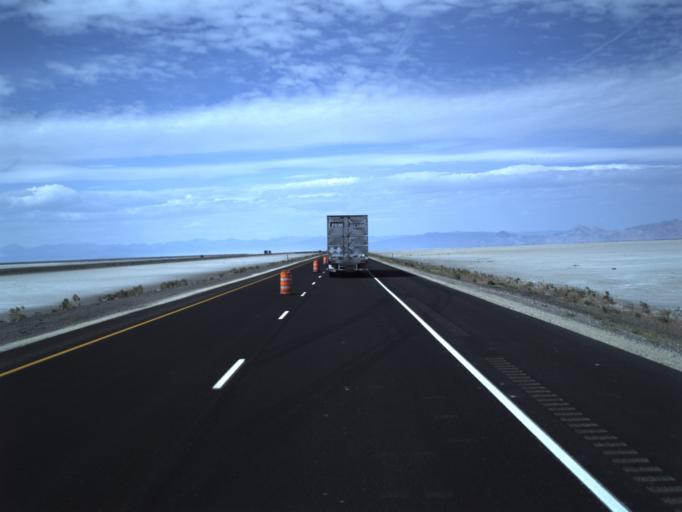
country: US
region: Utah
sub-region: Tooele County
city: Wendover
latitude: 40.7336
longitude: -113.5762
